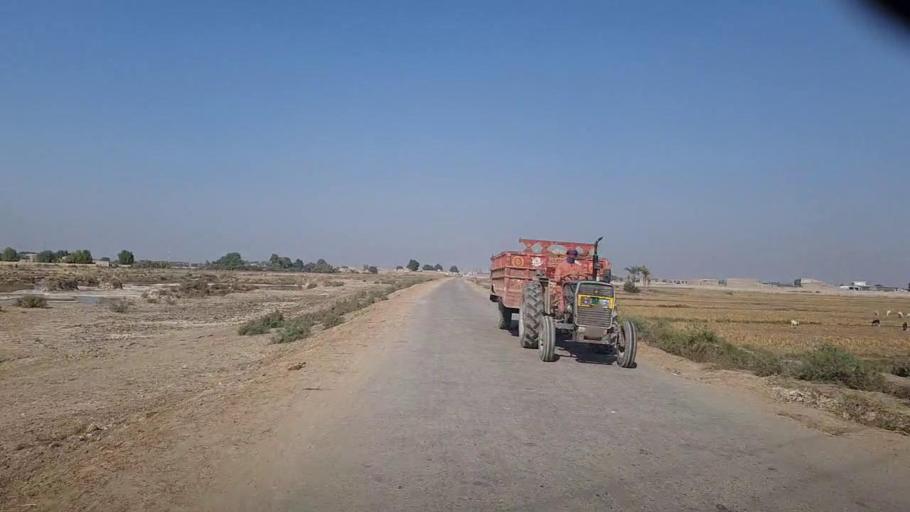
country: PK
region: Sindh
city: Tangwani
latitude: 28.2576
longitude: 68.9972
